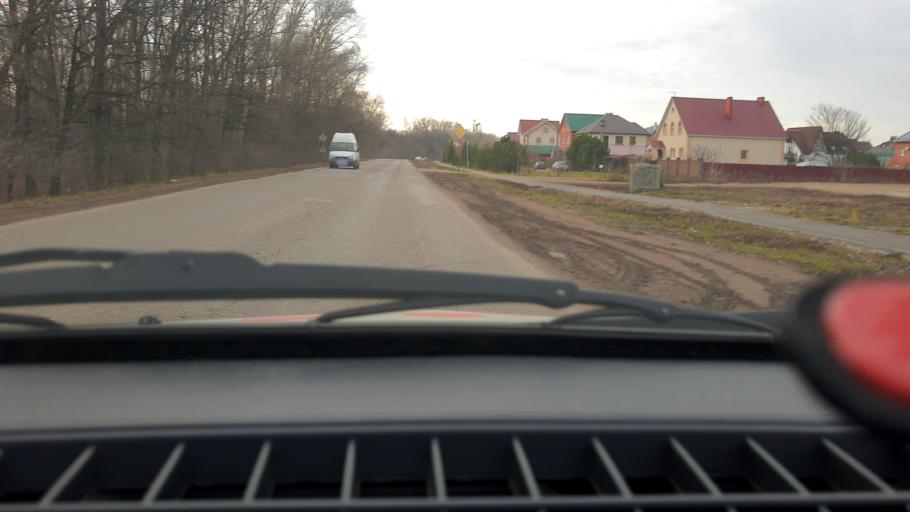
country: RU
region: Bashkortostan
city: Ufa
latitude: 54.7948
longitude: 55.9591
